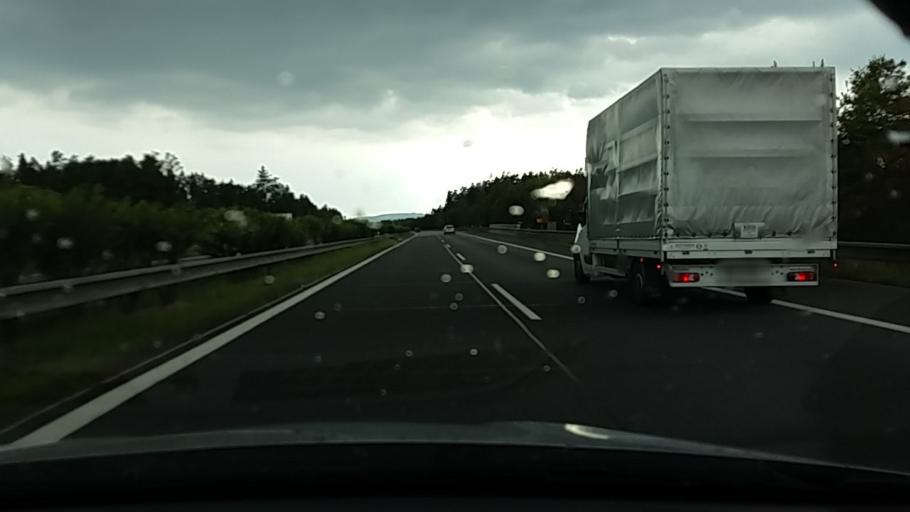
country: CZ
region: Plzensky
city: Bor
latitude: 49.7401
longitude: 12.7459
